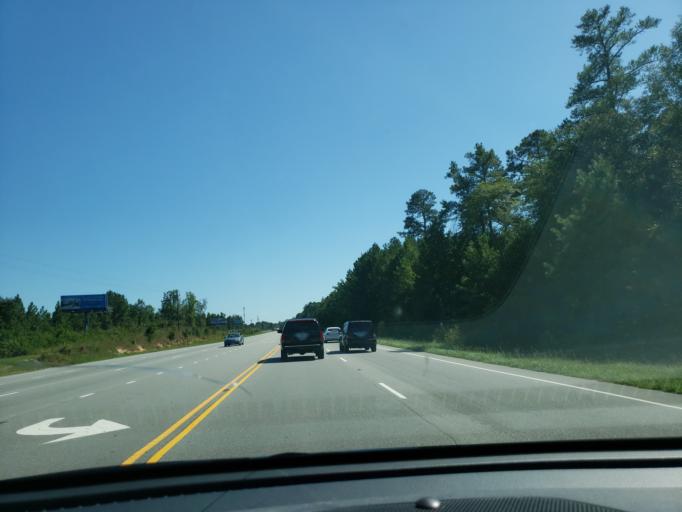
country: US
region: North Carolina
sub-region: Lee County
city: Broadway
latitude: 35.3588
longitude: -79.1098
